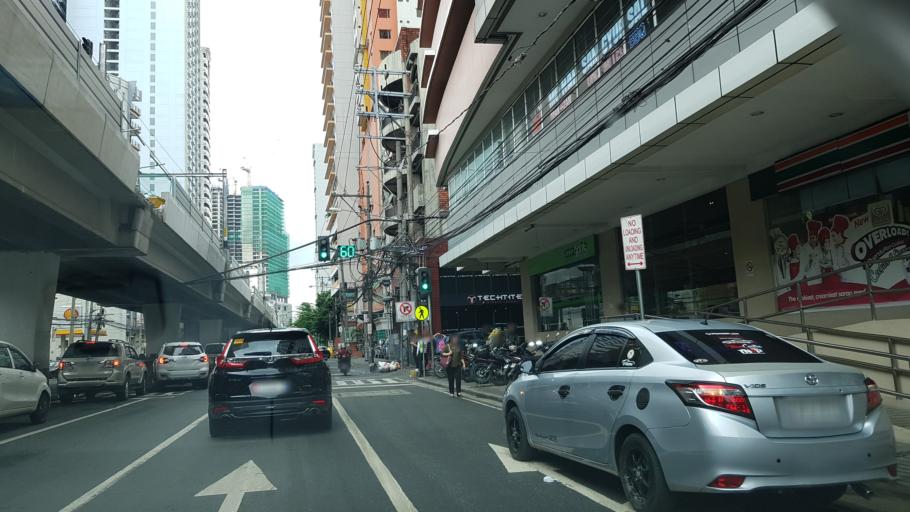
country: PH
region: Metro Manila
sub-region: City of Manila
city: Port Area
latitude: 14.5671
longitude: 120.9931
